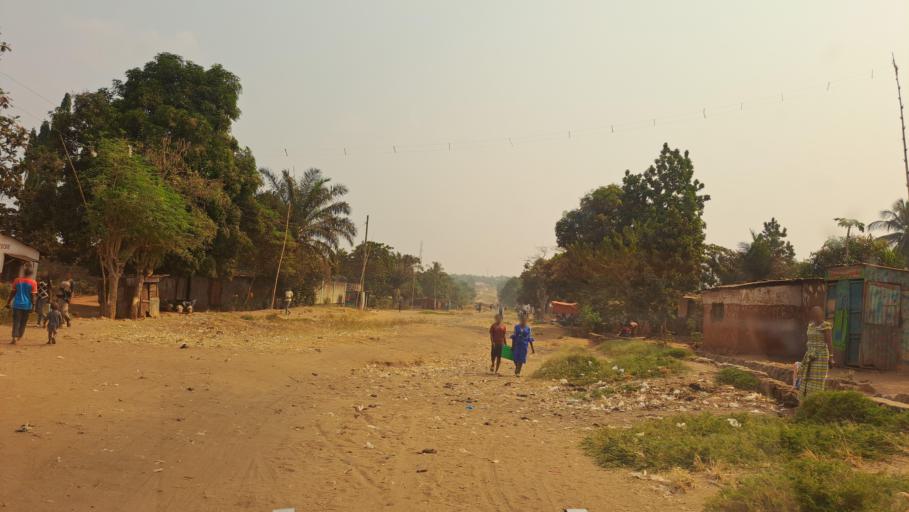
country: CD
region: Kasai-Oriental
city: Mbuji-Mayi
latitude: -6.1227
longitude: 23.6062
